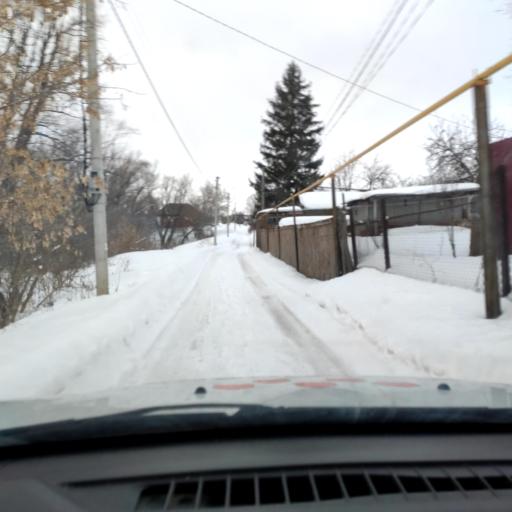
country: RU
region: Bashkortostan
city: Avdon
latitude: 54.6189
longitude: 55.6498
